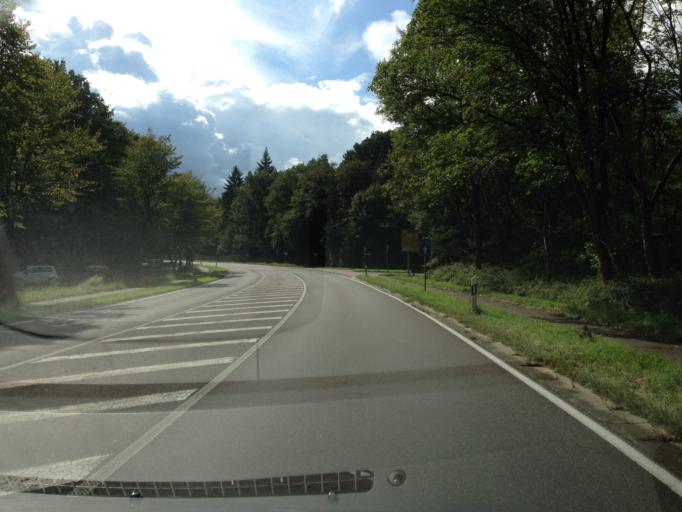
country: DE
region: North Rhine-Westphalia
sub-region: Regierungsbezirk Koln
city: Rath
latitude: 50.9103
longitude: 7.1004
